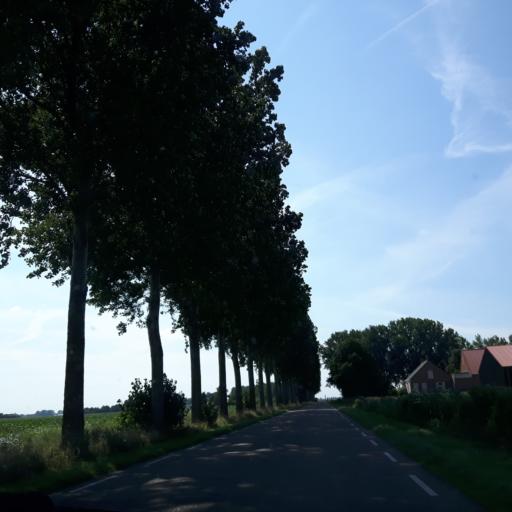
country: NL
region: North Brabant
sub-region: Gemeente Steenbergen
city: Nieuw-Vossemeer
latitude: 51.5618
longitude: 4.1882
